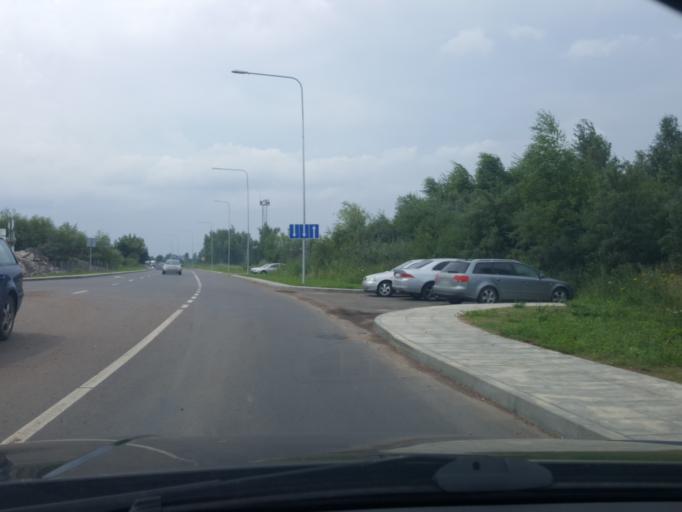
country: LT
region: Alytaus apskritis
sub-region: Alytus
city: Alytus
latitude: 54.4375
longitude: 24.0142
